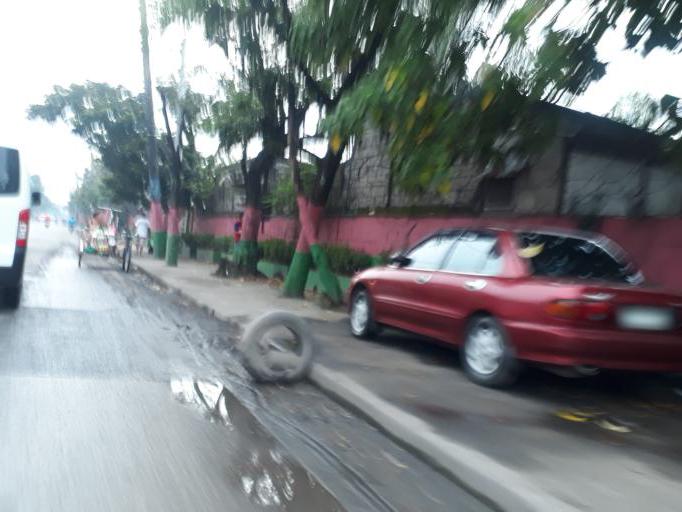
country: PH
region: Calabarzon
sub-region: Province of Rizal
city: Valenzuela
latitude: 14.6924
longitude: 120.9555
